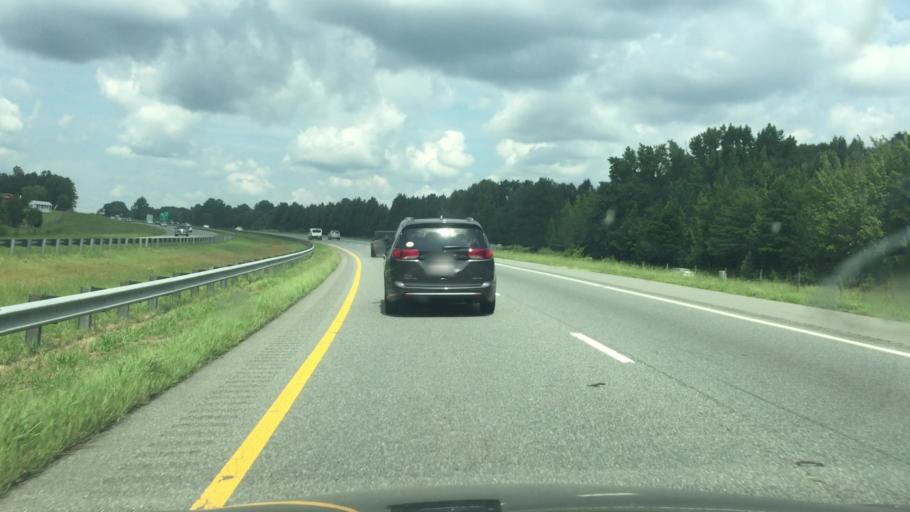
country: US
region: North Carolina
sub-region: Randolph County
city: Asheboro
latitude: 35.6120
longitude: -79.8192
